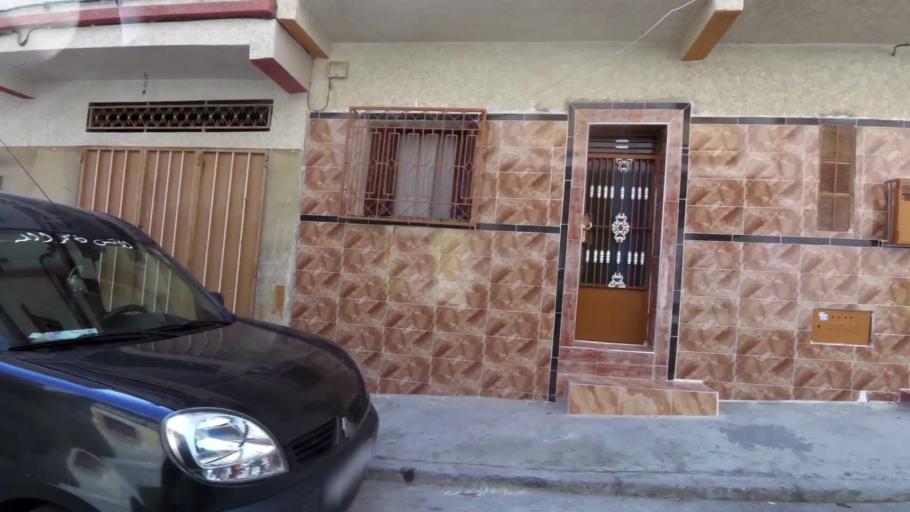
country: MA
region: Tanger-Tetouan
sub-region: Tanger-Assilah
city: Tangier
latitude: 35.7395
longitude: -5.8071
